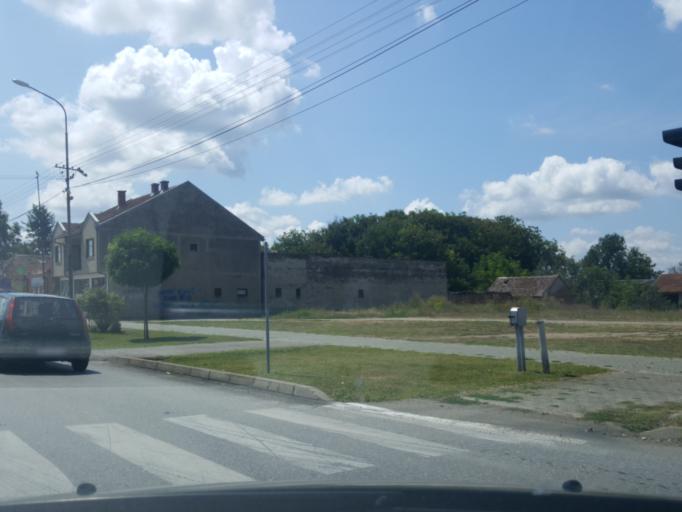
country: RS
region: Central Serbia
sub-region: Macvanski Okrug
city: Bogatic
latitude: 44.8416
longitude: 19.4815
